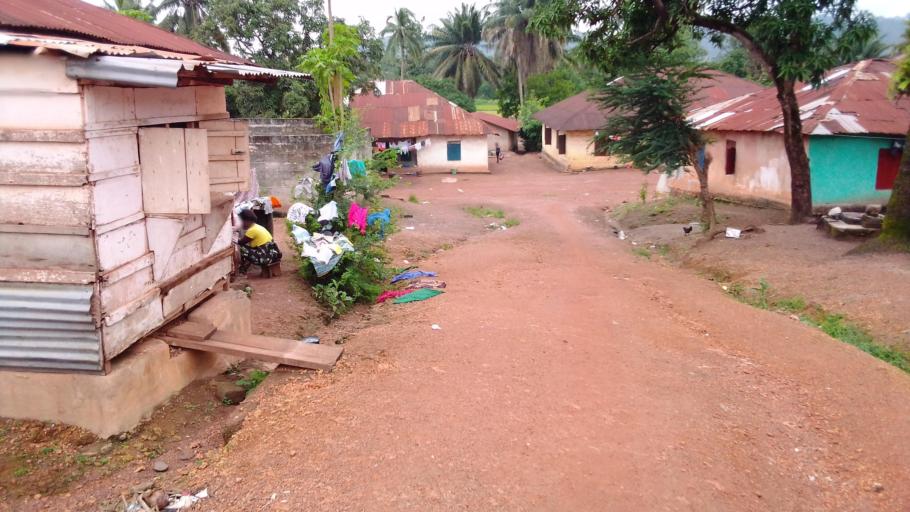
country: SL
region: Eastern Province
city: Kenema
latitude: 7.8634
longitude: -11.1885
